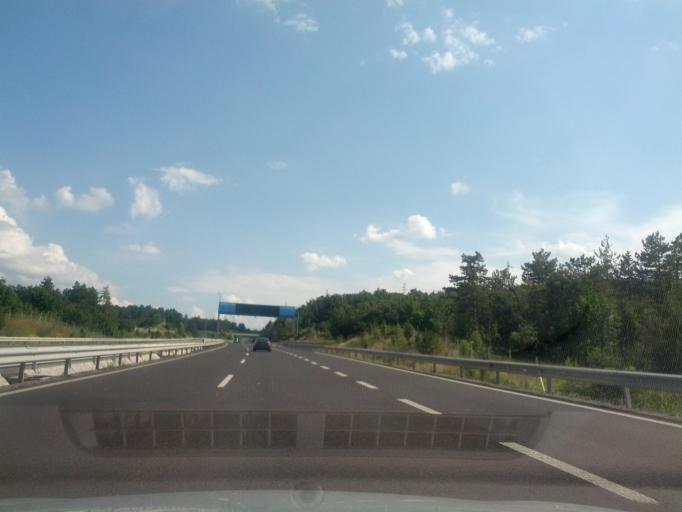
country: SI
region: Divaca
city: Divaca
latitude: 45.6456
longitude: 13.9598
